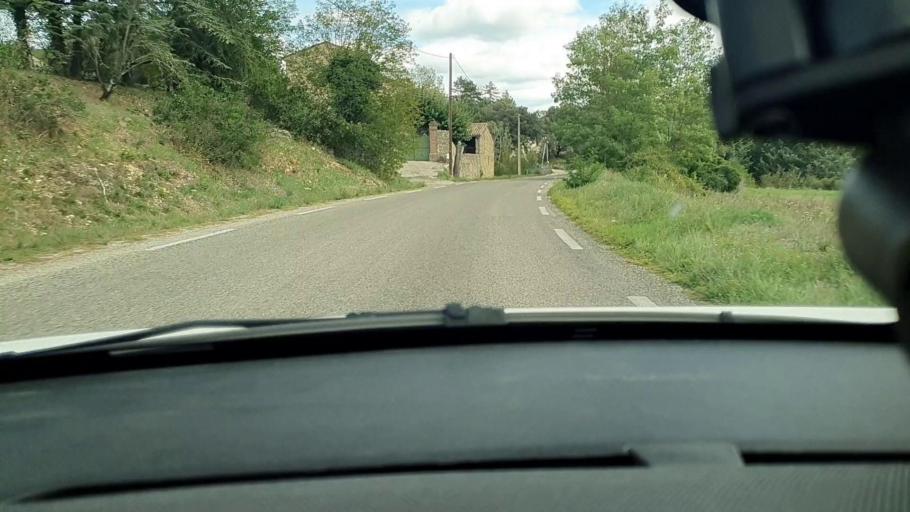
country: FR
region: Languedoc-Roussillon
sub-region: Departement du Gard
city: Les Mages
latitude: 44.2153
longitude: 4.1822
